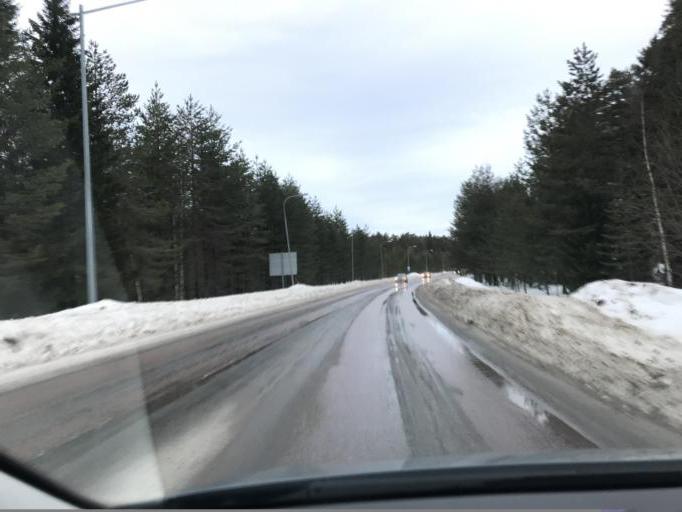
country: SE
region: Norrbotten
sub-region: Lulea Kommun
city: Gammelstad
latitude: 65.6192
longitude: 22.0367
